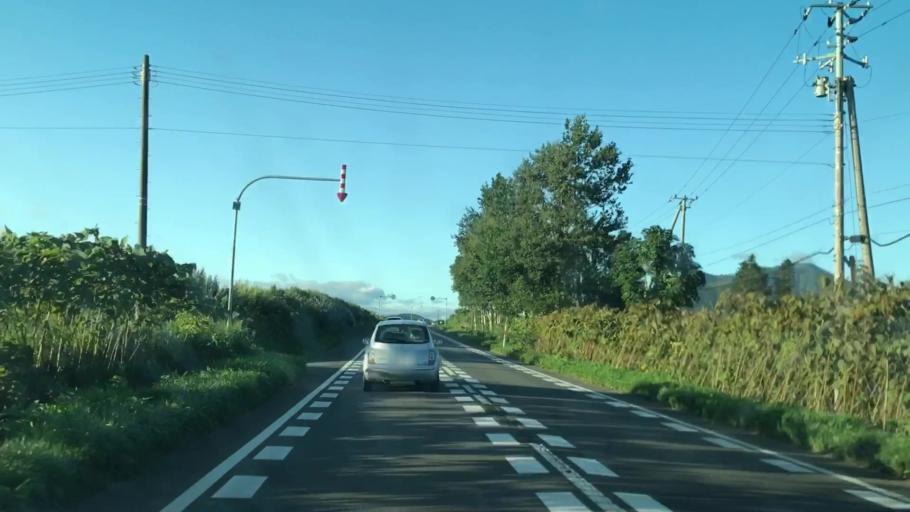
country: JP
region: Hokkaido
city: Niseko Town
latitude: 42.7155
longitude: 140.8589
